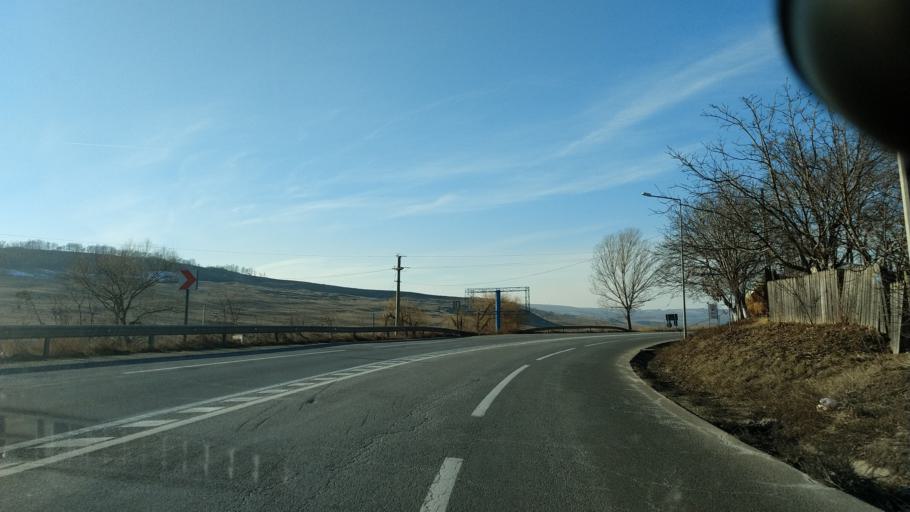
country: RO
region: Iasi
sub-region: Comuna Targu Frumos
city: Targu Frumos
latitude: 47.1952
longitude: 26.9962
